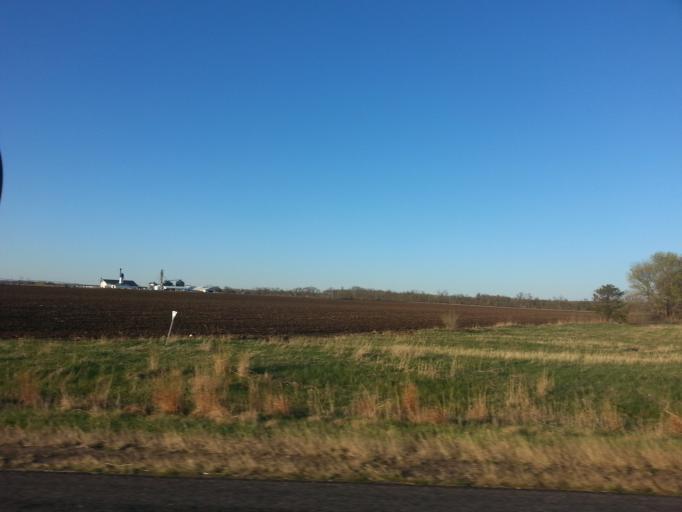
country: US
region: Wisconsin
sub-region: Pierce County
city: Prescott
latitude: 44.6803
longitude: -92.7996
